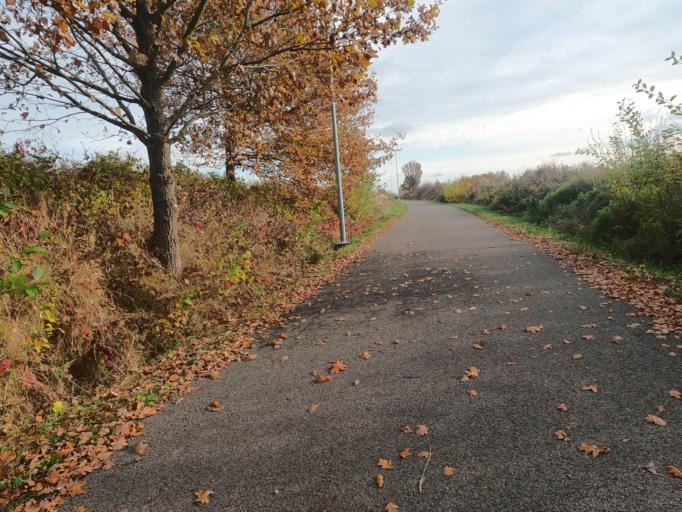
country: PL
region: Pomeranian Voivodeship
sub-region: Powiat starogardzki
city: Starogard Gdanski
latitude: 53.9803
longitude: 18.4786
